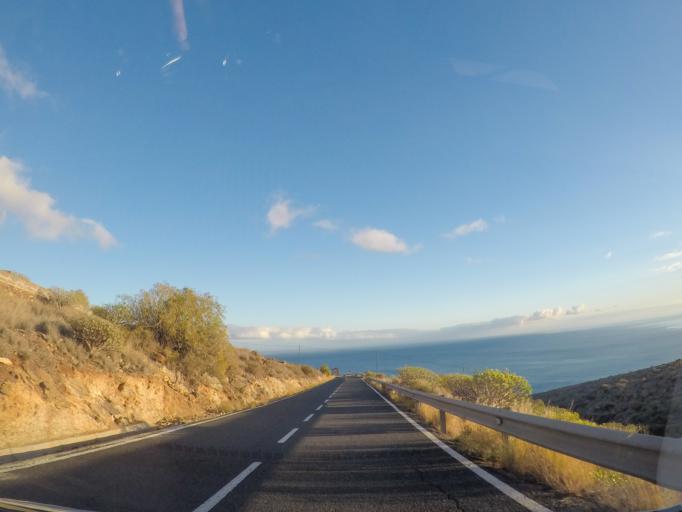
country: ES
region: Canary Islands
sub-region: Provincia de Santa Cruz de Tenerife
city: Alajero
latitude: 28.0393
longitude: -17.2262
